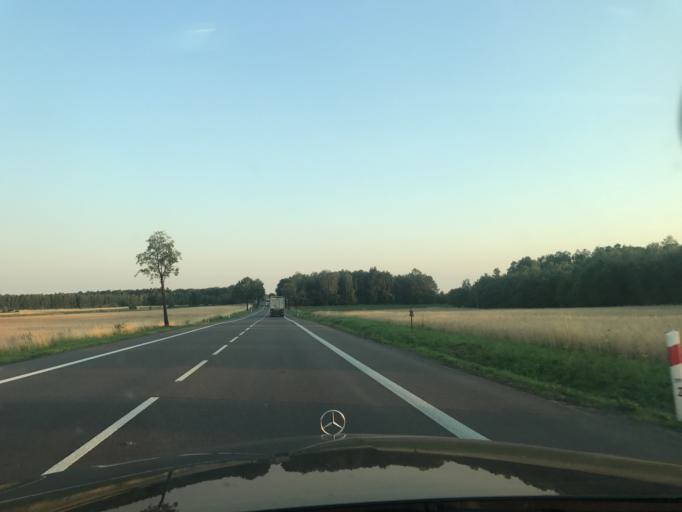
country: PL
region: Lublin Voivodeship
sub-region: Powiat lubartowski
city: Serniki
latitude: 51.4087
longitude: 22.6389
